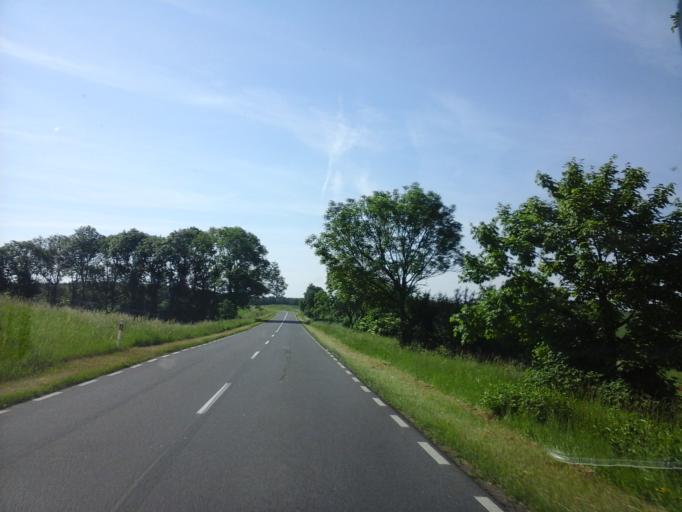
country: PL
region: West Pomeranian Voivodeship
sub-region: Powiat choszczenski
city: Bierzwnik
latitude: 53.0993
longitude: 15.6326
